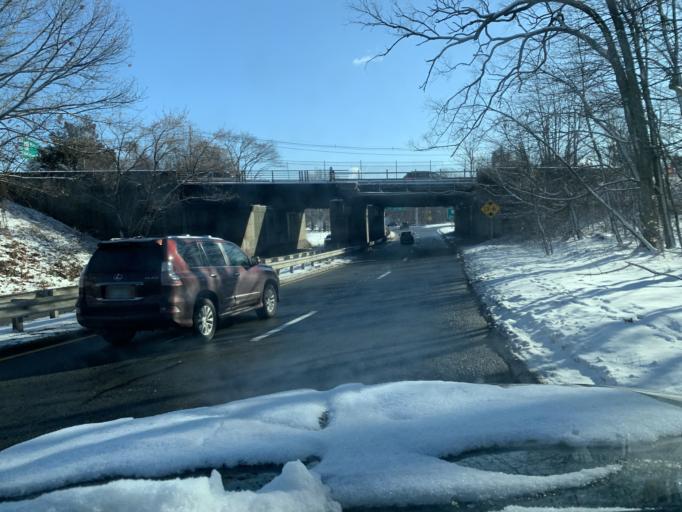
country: US
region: Massachusetts
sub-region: Essex County
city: Danvers
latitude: 42.5610
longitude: -70.9781
